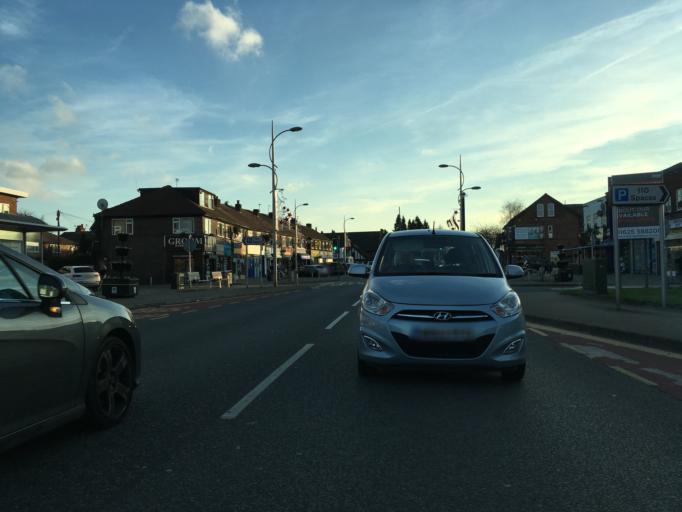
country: GB
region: England
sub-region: Cheshire East
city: Wilmslow
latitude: 53.3499
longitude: -2.2153
